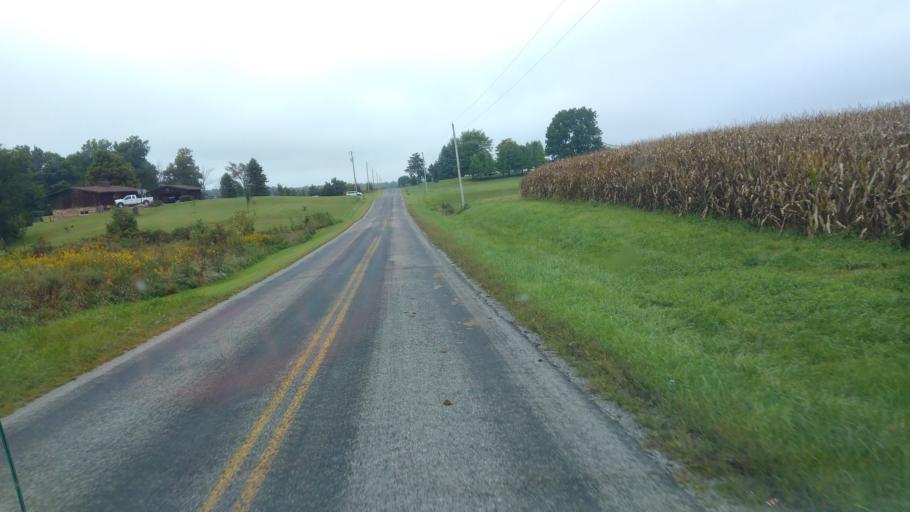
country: US
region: Ohio
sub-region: Hardin County
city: Kenton
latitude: 40.5579
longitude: -83.6361
